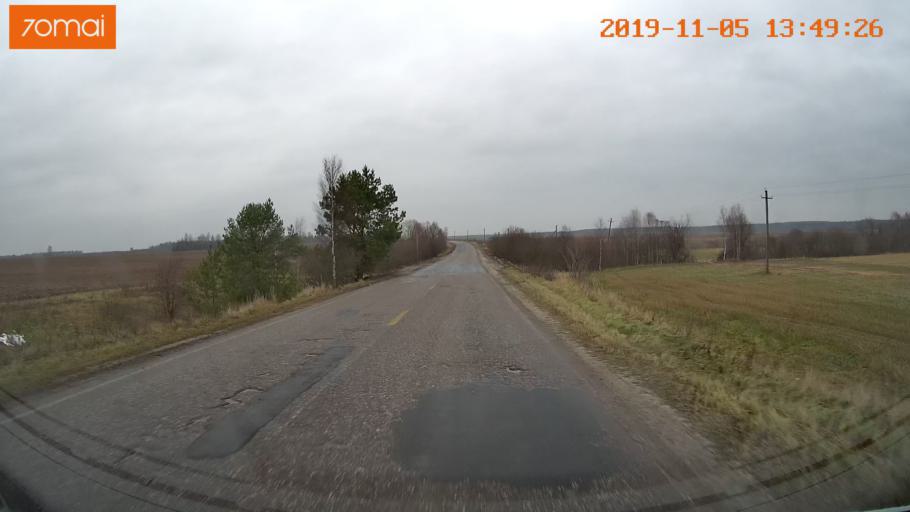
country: RU
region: Ivanovo
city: Kaminskiy
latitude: 57.0106
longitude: 41.4096
